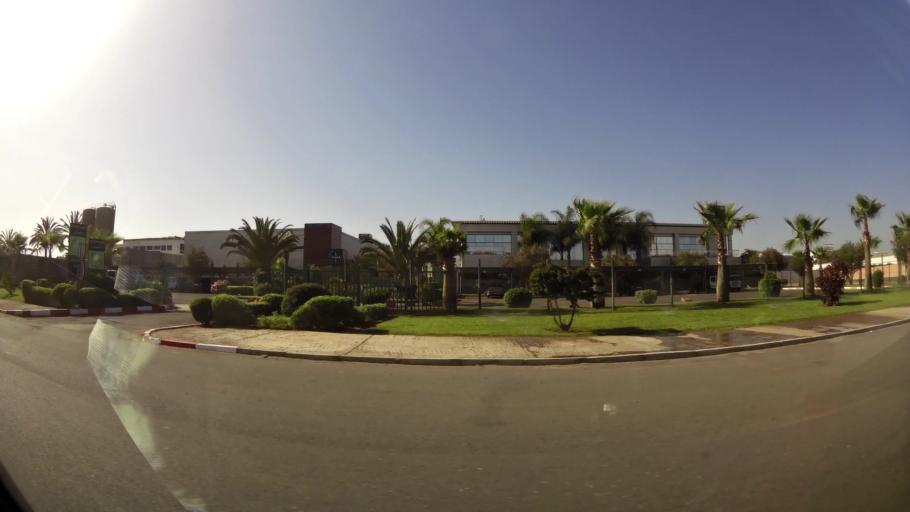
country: MA
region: Souss-Massa-Draa
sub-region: Inezgane-Ait Mellou
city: Inezgane
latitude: 30.3813
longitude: -9.5158
